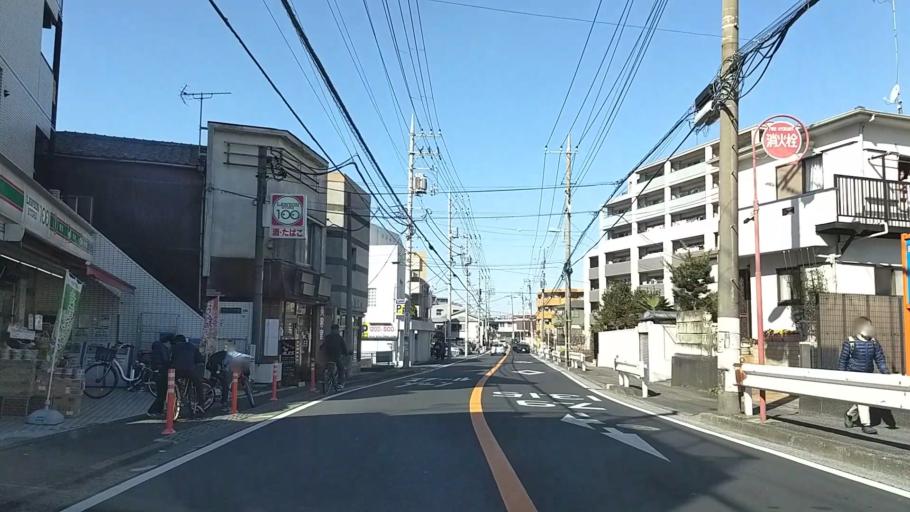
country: JP
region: Kanagawa
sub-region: Kawasaki-shi
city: Kawasaki
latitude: 35.5133
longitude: 139.6580
